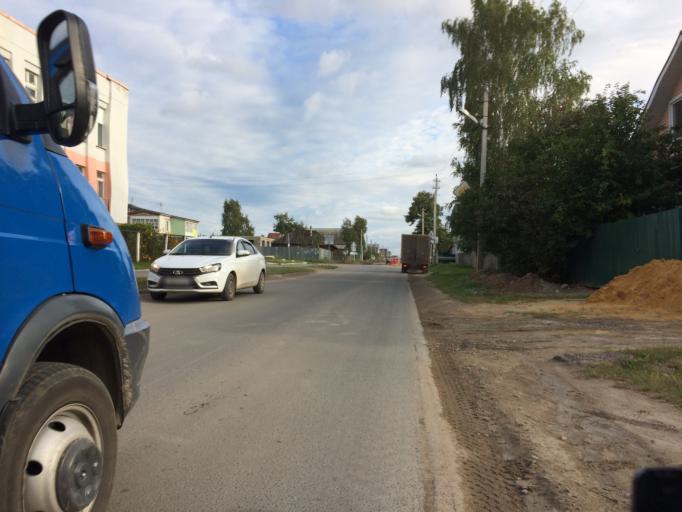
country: RU
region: Mariy-El
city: Yoshkar-Ola
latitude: 56.6472
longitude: 47.9812
